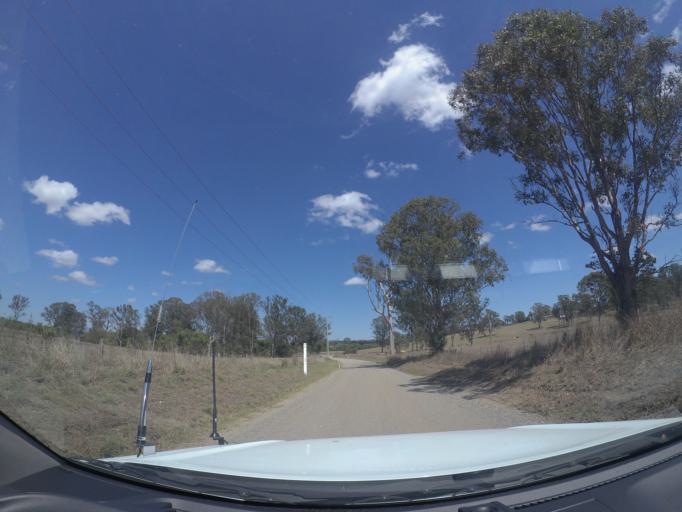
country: AU
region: Queensland
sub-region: Logan
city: Cedar Vale
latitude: -27.8392
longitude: 152.9196
